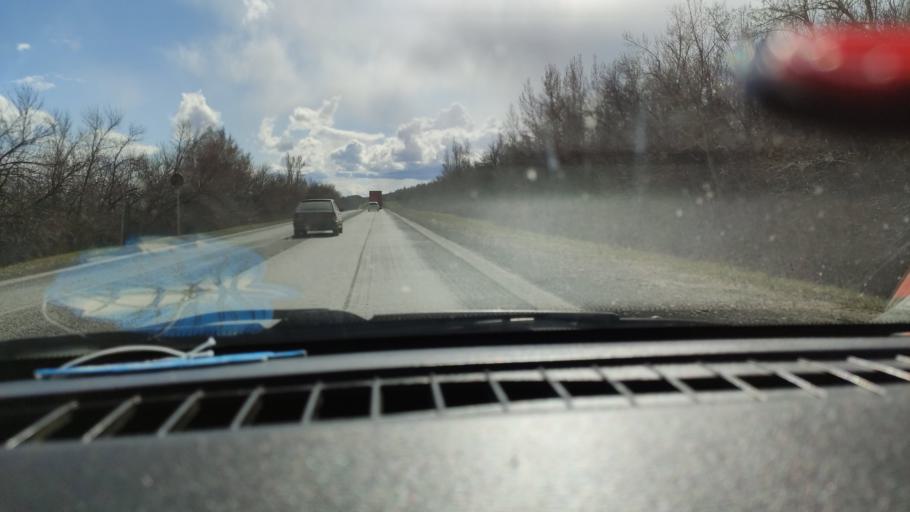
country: RU
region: Saratov
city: Dukhovnitskoye
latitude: 52.6545
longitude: 48.2039
